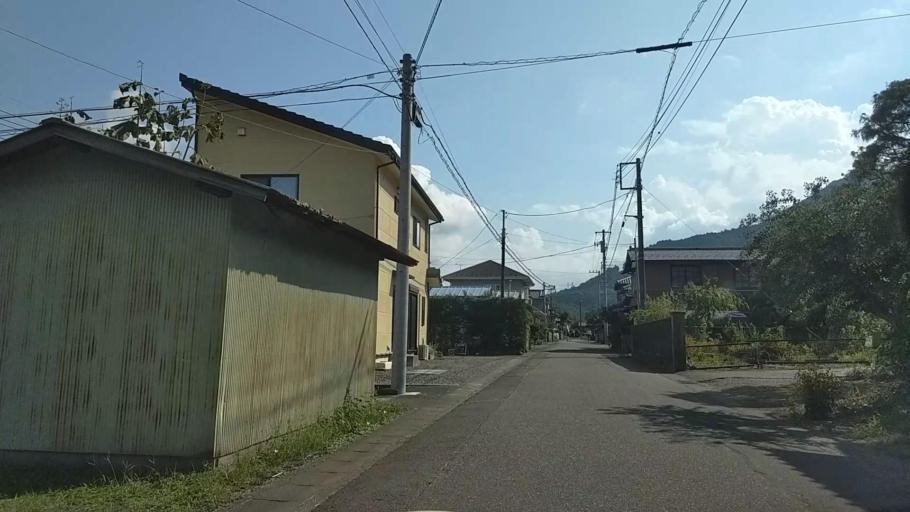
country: JP
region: Yamanashi
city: Ryuo
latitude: 35.4123
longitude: 138.4420
